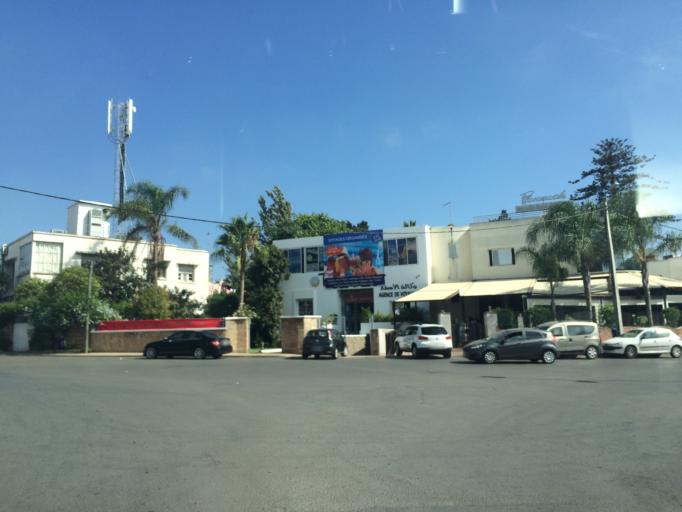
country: MA
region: Rabat-Sale-Zemmour-Zaer
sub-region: Rabat
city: Rabat
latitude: 33.9906
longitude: -6.8259
